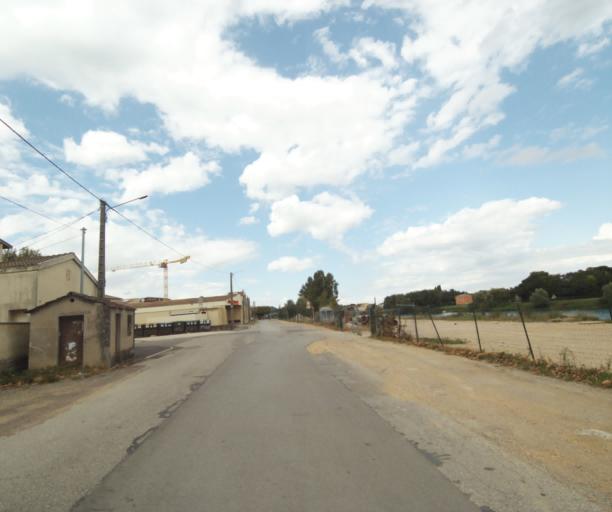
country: FR
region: Bourgogne
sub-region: Departement de Saone-et-Loire
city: Tournus
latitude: 46.5581
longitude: 4.9167
